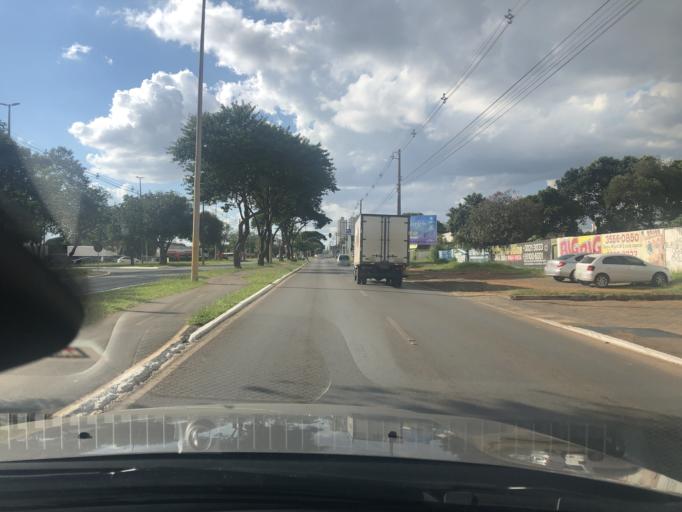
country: BR
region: Federal District
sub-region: Brasilia
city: Brasilia
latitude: -16.0102
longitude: -48.0598
